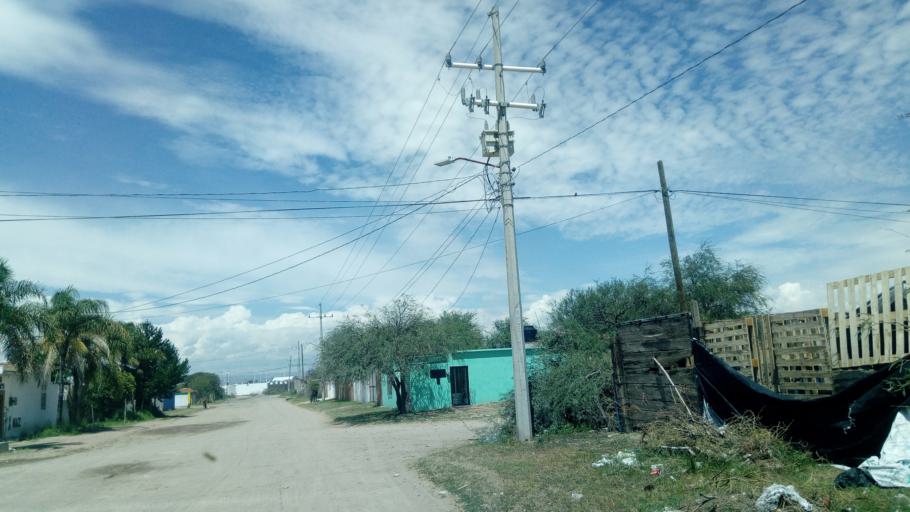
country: MX
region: Durango
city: Victoria de Durango
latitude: 24.0166
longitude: -104.5907
